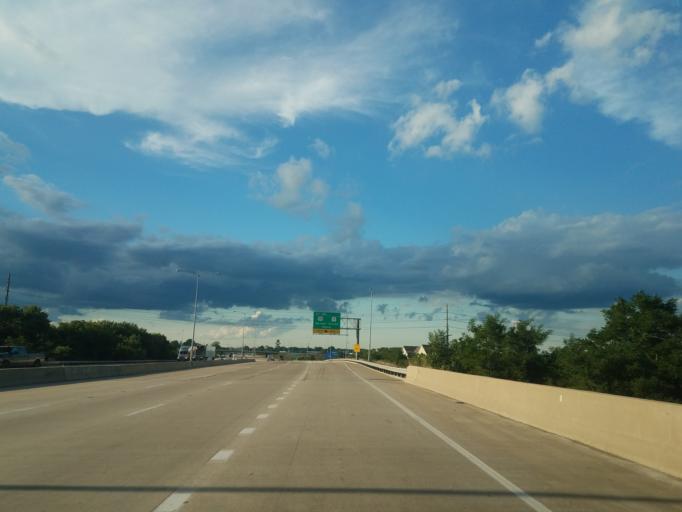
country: US
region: Illinois
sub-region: McLean County
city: Bloomington
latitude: 40.4793
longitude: -89.0286
